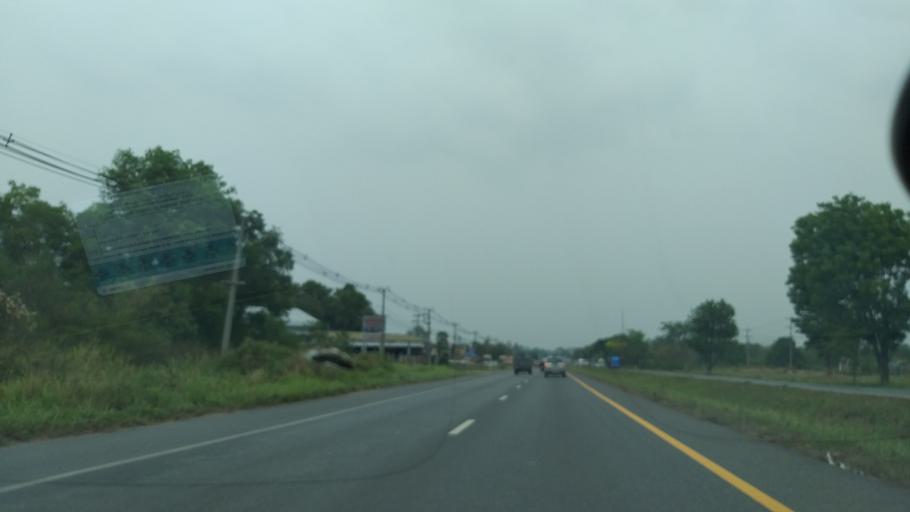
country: TH
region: Chon Buri
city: Ko Chan
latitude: 13.3099
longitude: 101.2652
